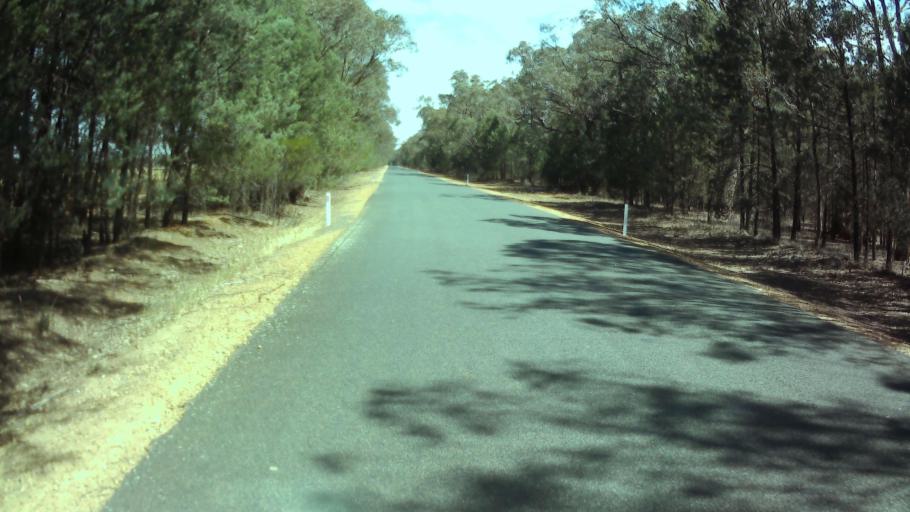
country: AU
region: New South Wales
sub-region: Weddin
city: Grenfell
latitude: -34.0142
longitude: 148.1288
